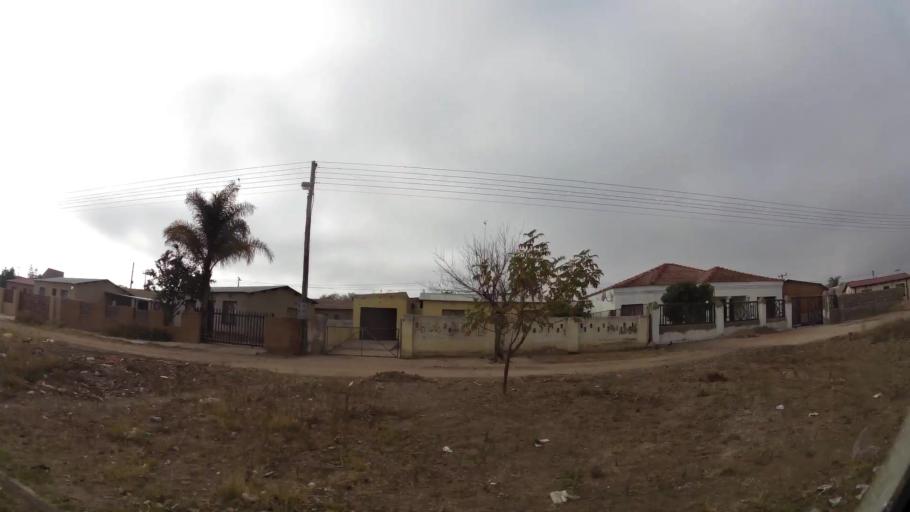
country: ZA
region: Limpopo
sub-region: Capricorn District Municipality
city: Polokwane
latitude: -23.8368
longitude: 29.3815
